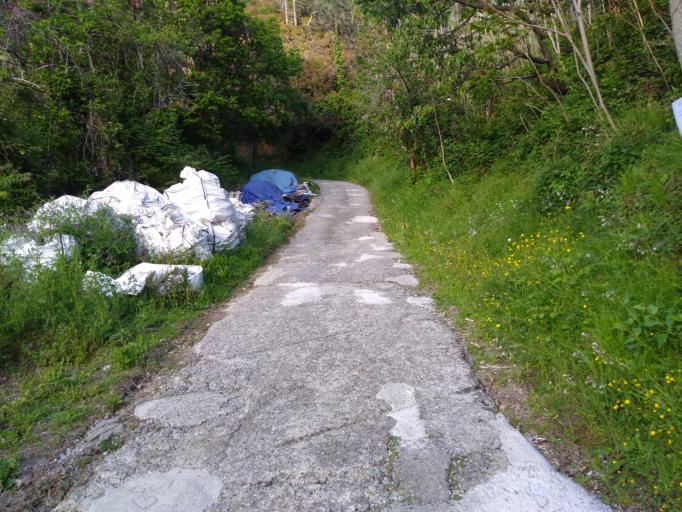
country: IT
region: Liguria
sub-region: Provincia di La Spezia
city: Monterosso al Mare
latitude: 44.1541
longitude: 9.6572
